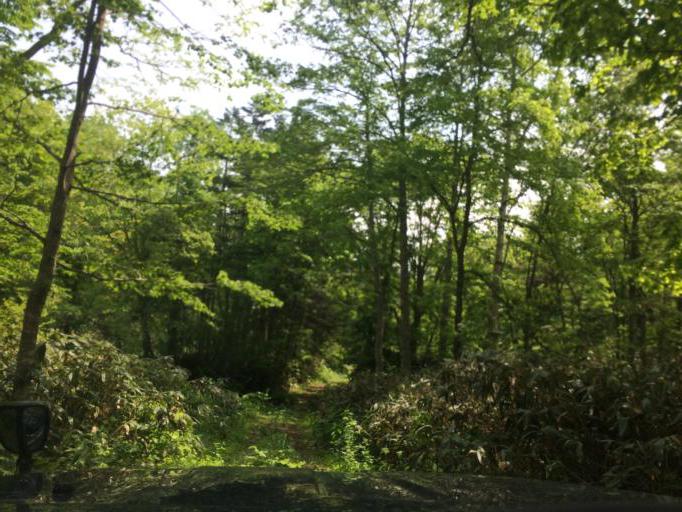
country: JP
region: Hokkaido
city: Niseko Town
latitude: 42.7174
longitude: 140.5528
